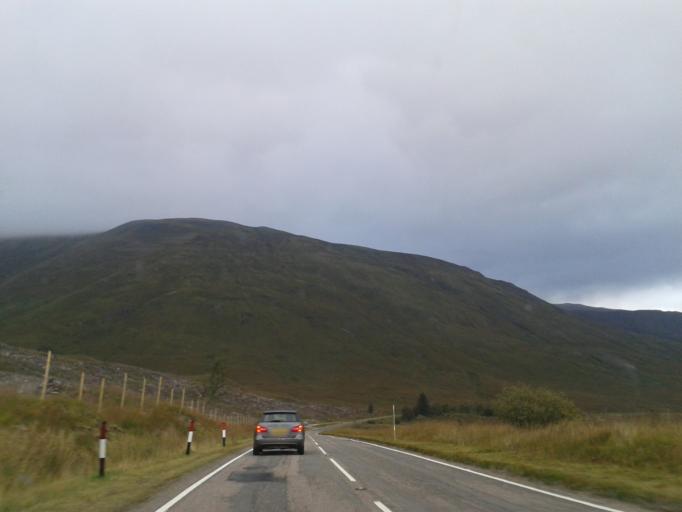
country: GB
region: Scotland
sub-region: Highland
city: Fort William
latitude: 57.1579
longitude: -5.1699
